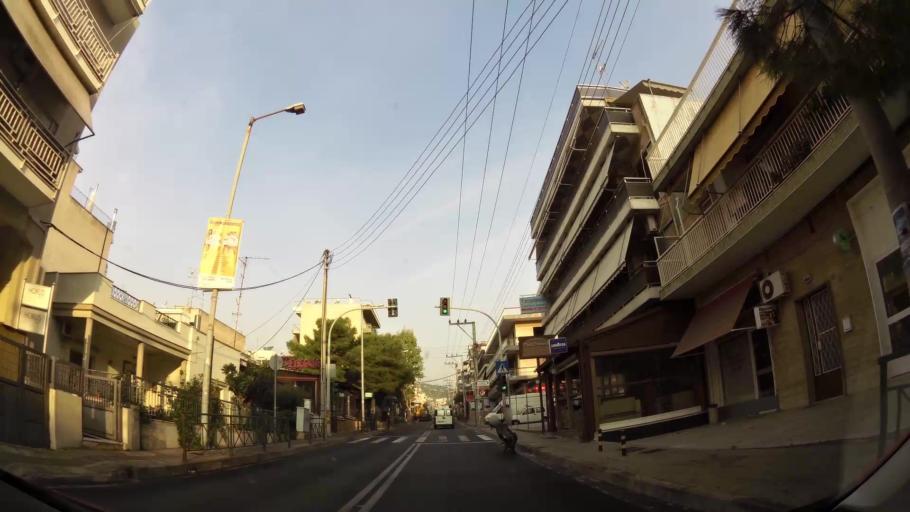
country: GR
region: Attica
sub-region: Nomarchia Athinas
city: Petroupolis
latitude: 38.0357
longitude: 23.6770
